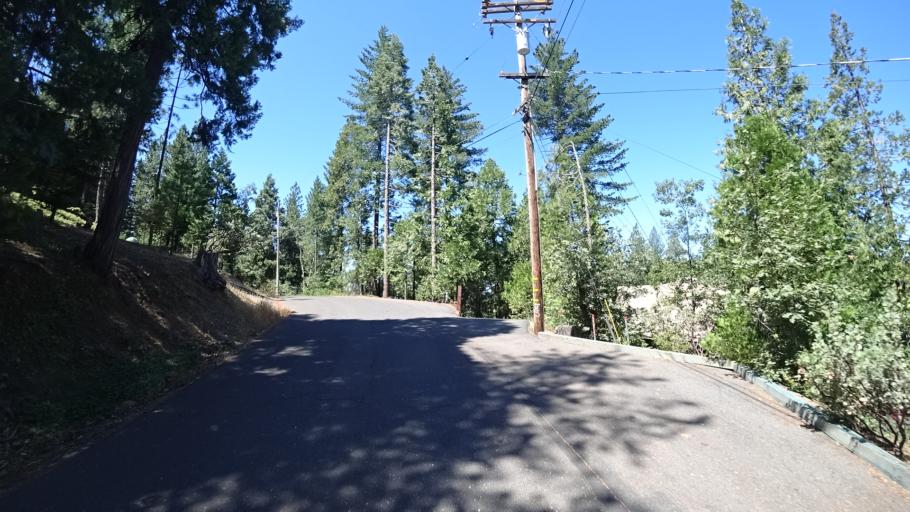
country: US
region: California
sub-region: Calaveras County
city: Arnold
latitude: 38.2273
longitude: -120.3770
